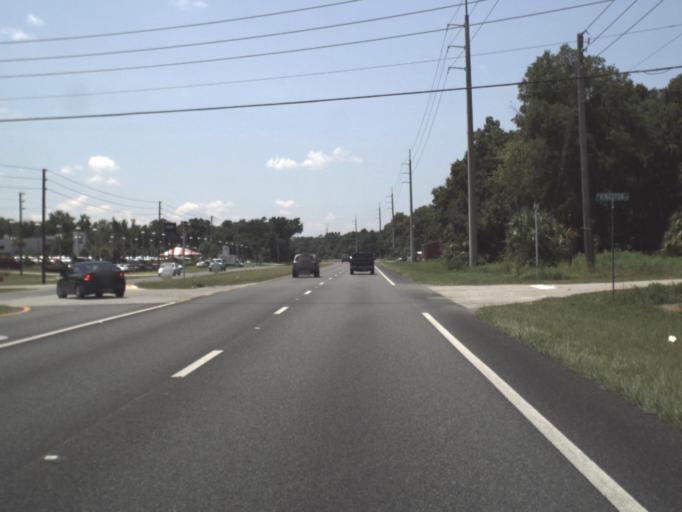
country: US
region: Florida
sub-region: Citrus County
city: Homosassa Springs
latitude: 28.8296
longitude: -82.5795
